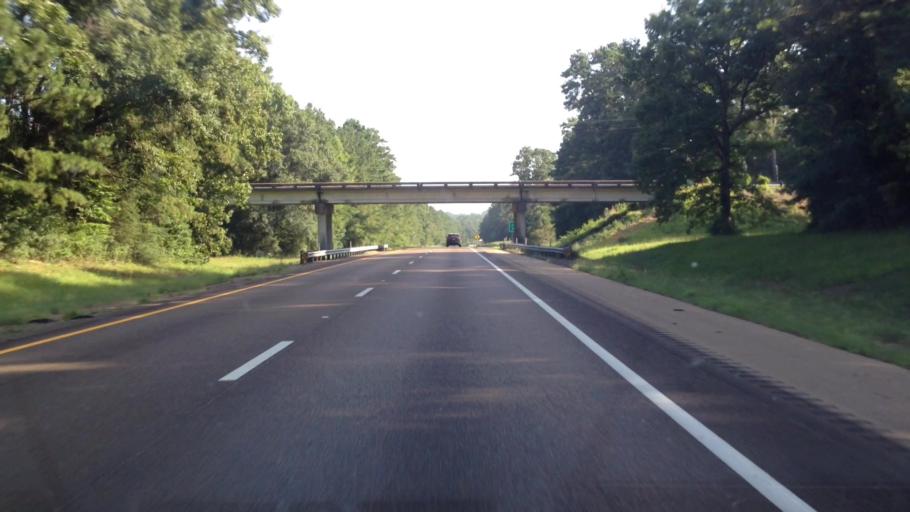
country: US
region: Mississippi
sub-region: Pike County
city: Summit
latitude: 31.3483
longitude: -90.4785
